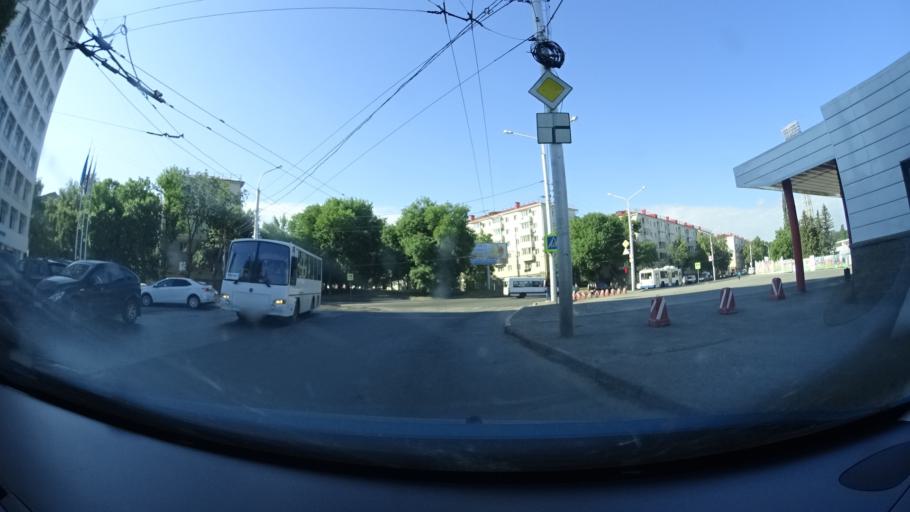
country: RU
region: Bashkortostan
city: Ufa
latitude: 54.8259
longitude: 56.0647
